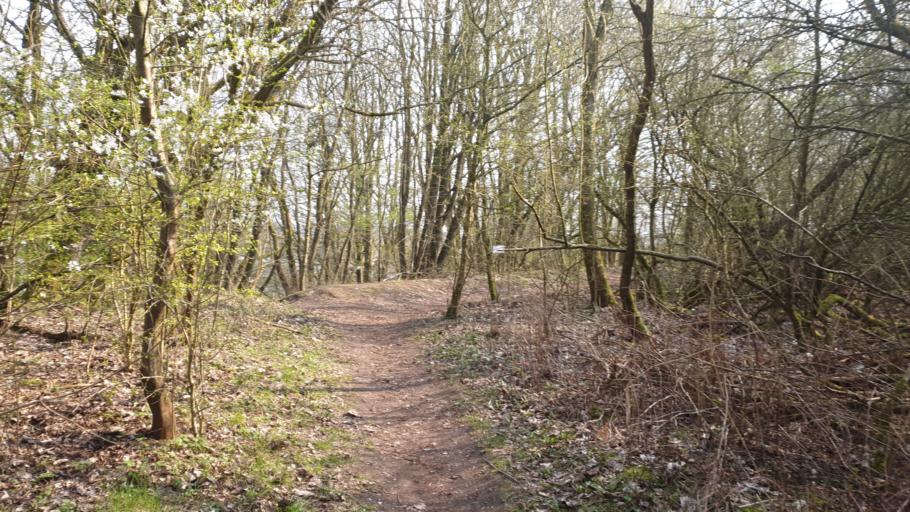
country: DK
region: Central Jutland
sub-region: Hedensted Kommune
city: Hedensted
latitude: 55.8112
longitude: 9.7031
